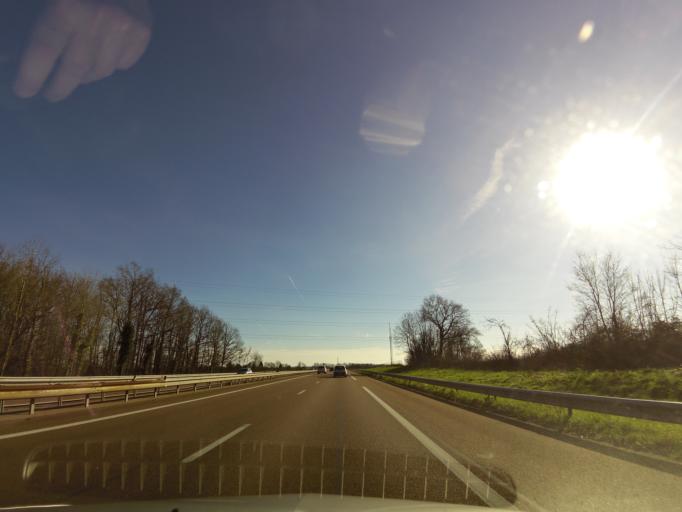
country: FR
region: Bourgogne
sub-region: Departement de l'Yonne
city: Venoy
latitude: 47.8105
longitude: 3.6278
